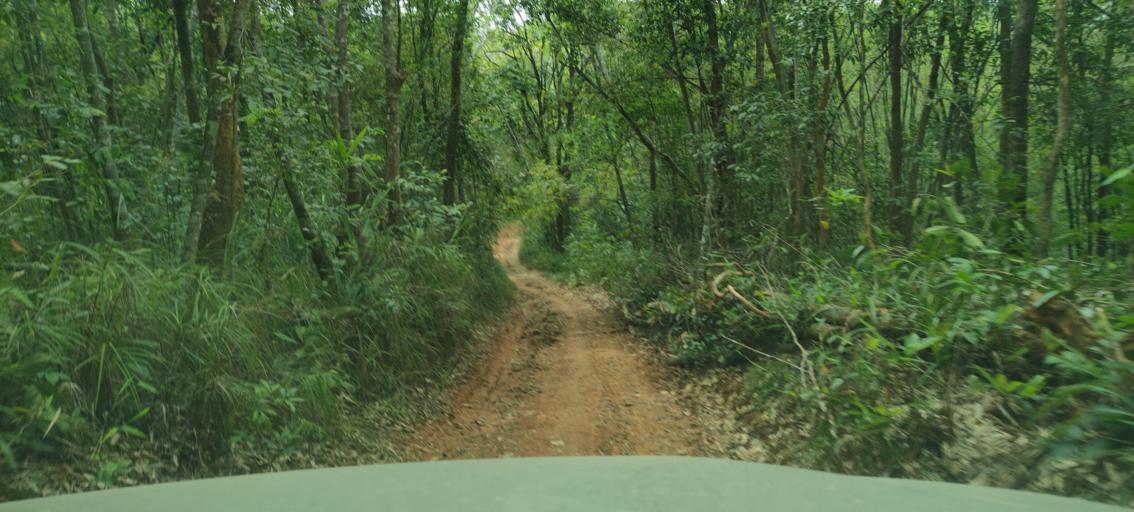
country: LA
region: Loungnamtha
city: Muang Nale
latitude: 20.4138
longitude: 101.4841
